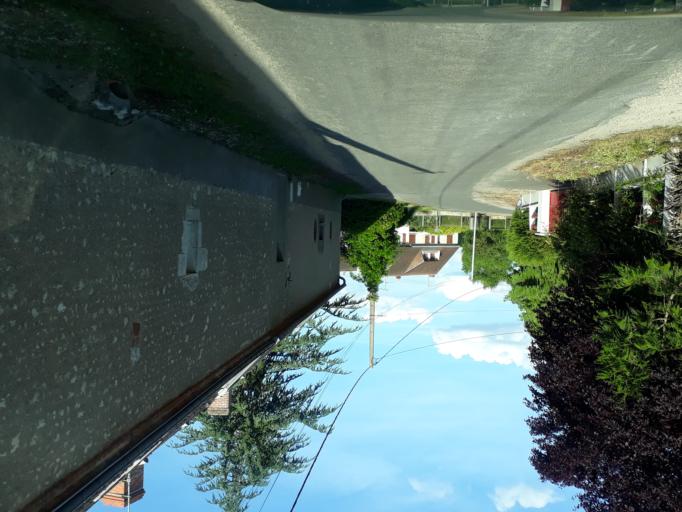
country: FR
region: Centre
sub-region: Departement du Loiret
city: Saint-Hilaire-Saint-Mesmin
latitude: 47.8437
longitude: 1.8146
